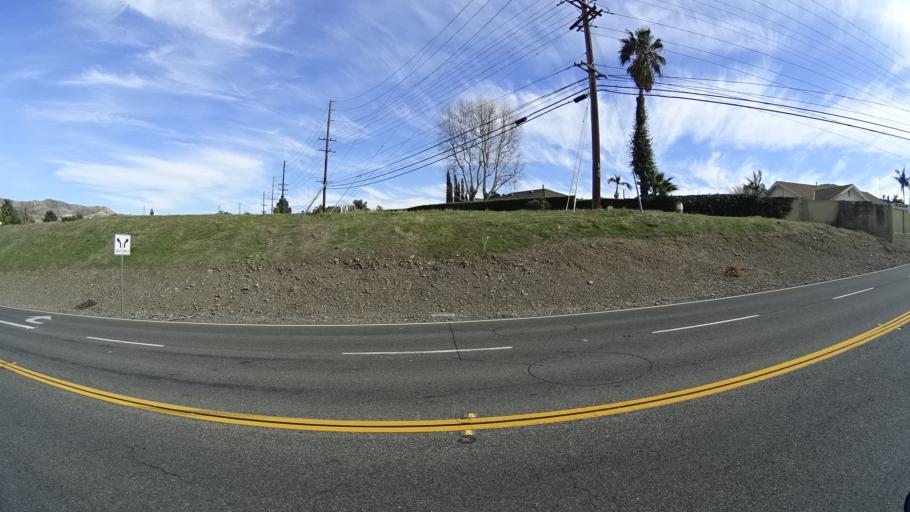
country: US
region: California
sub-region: Orange County
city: Villa Park
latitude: 33.8092
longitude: -117.8012
